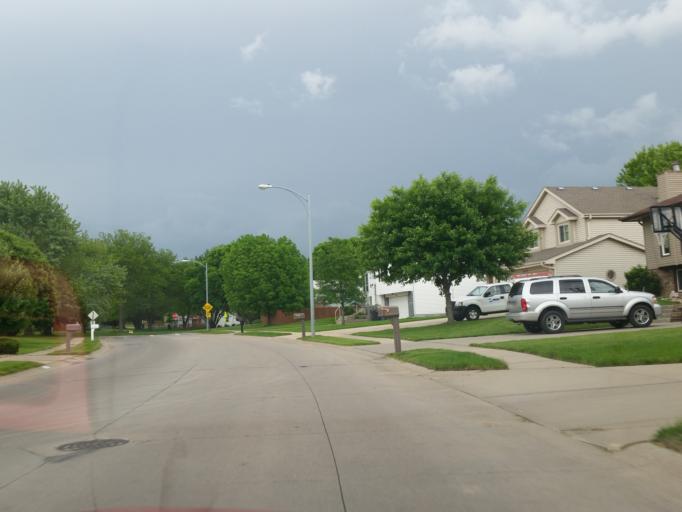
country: US
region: Nebraska
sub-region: Sarpy County
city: Offutt Air Force Base
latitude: 41.1492
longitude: -95.9464
